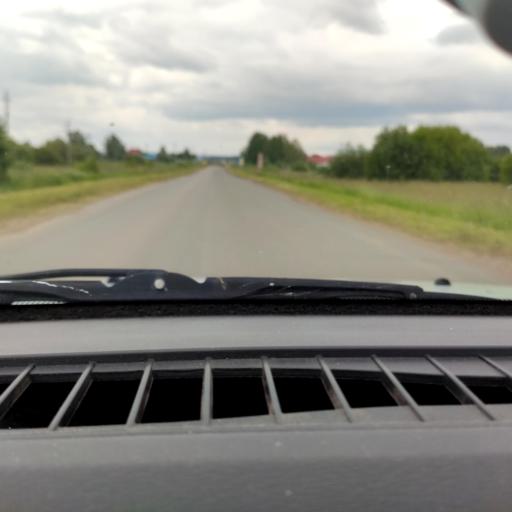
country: RU
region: Perm
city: Uinskoye
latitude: 57.0968
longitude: 56.6432
